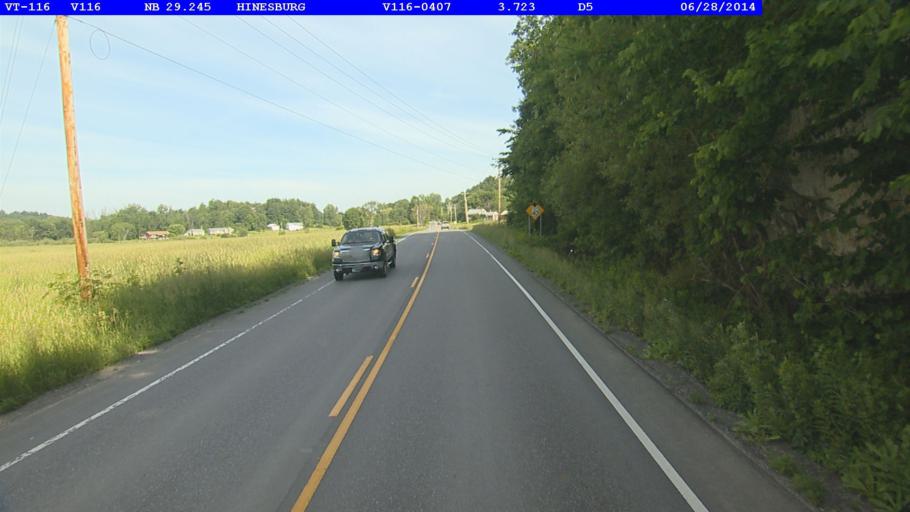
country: US
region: Vermont
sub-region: Chittenden County
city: Hinesburg
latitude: 44.3232
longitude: -73.0988
